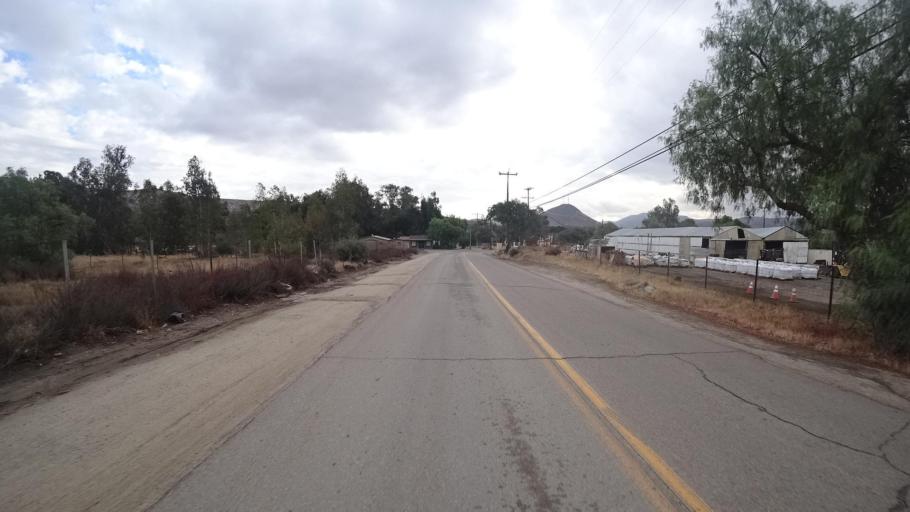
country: MX
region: Baja California
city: Tecate
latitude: 32.5826
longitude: -116.6222
